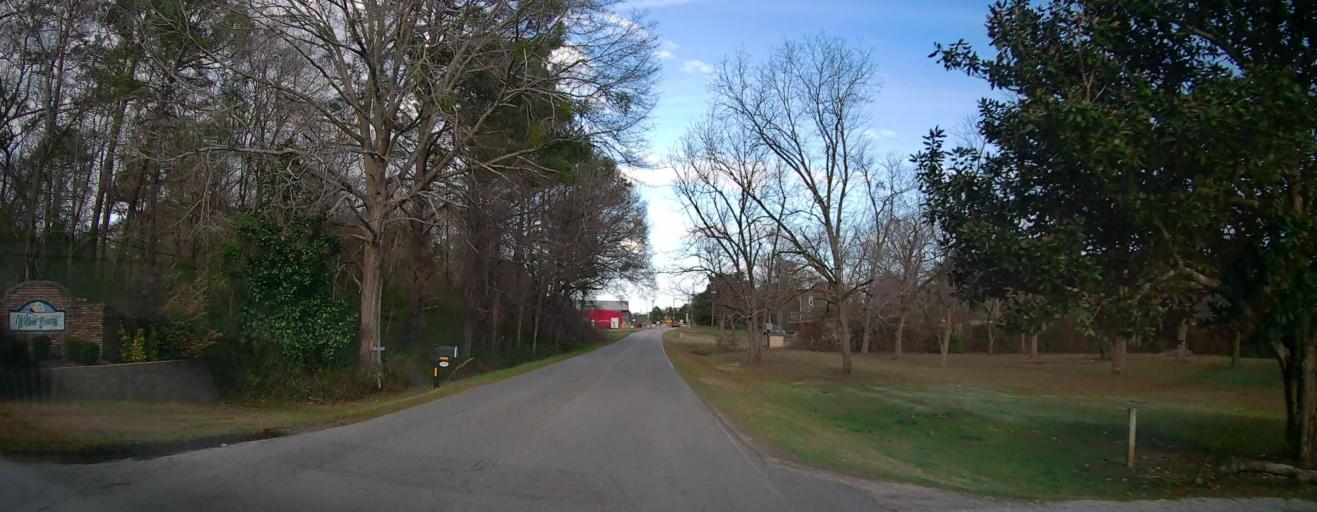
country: US
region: Georgia
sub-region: Harris County
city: Hamilton
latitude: 32.6305
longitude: -84.8051
